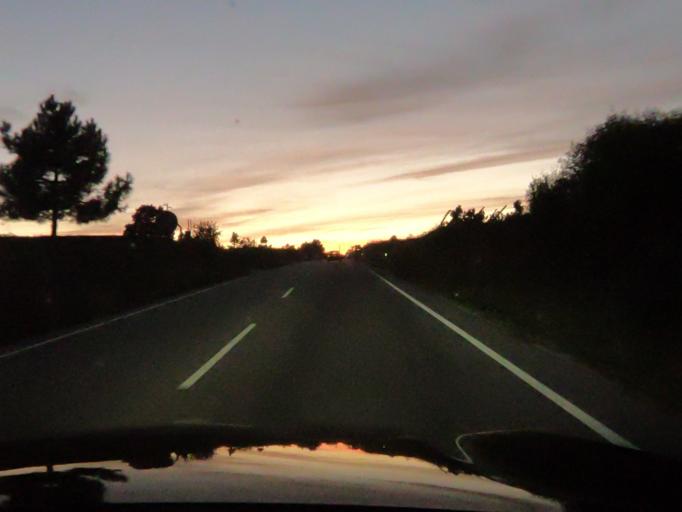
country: PT
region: Vila Real
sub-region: Sabrosa
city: Sabrosa
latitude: 41.2622
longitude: -7.6139
